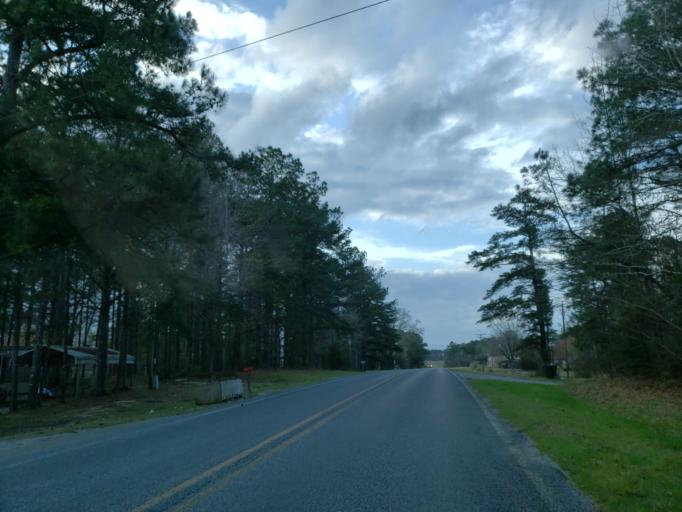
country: US
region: Mississippi
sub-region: Clarke County
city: Stonewall
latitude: 32.2064
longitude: -88.6910
